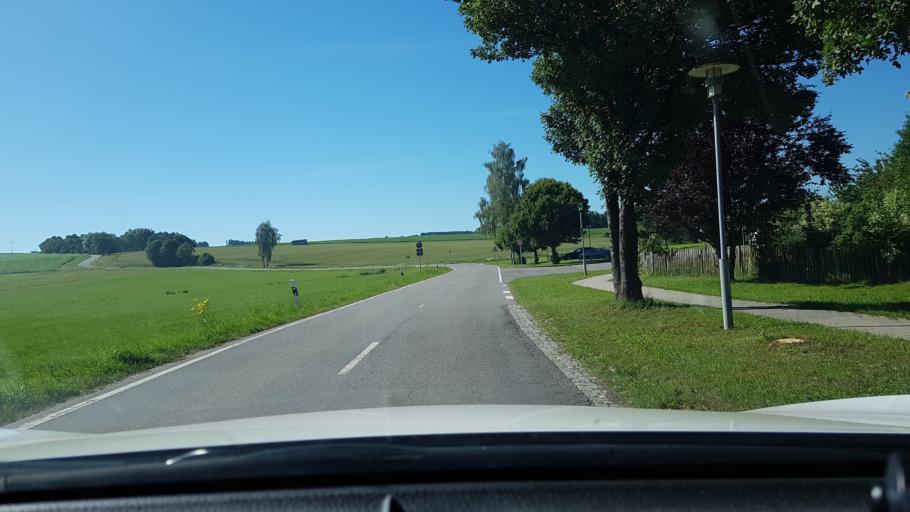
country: DE
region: Baden-Wuerttemberg
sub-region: Tuebingen Region
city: Gutenzell-Hurbel
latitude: 48.1074
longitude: 9.9503
